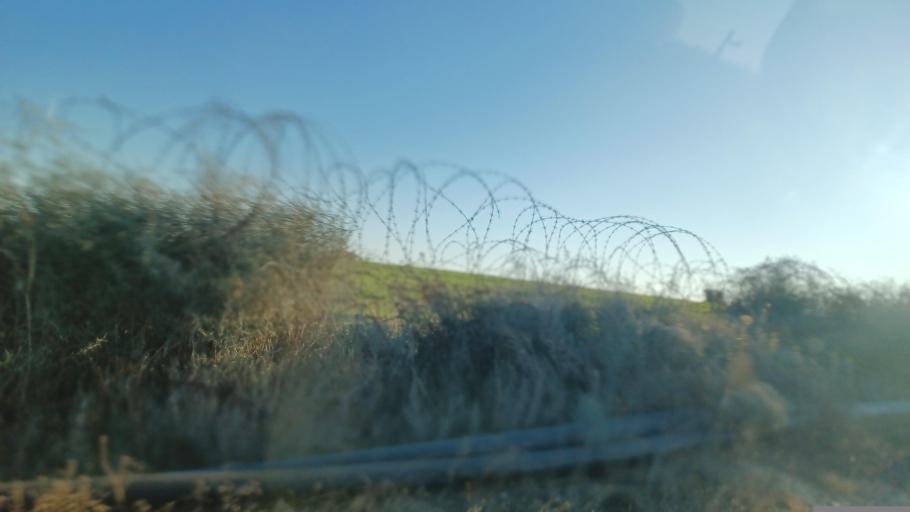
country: CY
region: Lefkosia
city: Kato Deftera
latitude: 35.1419
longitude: 33.2746
